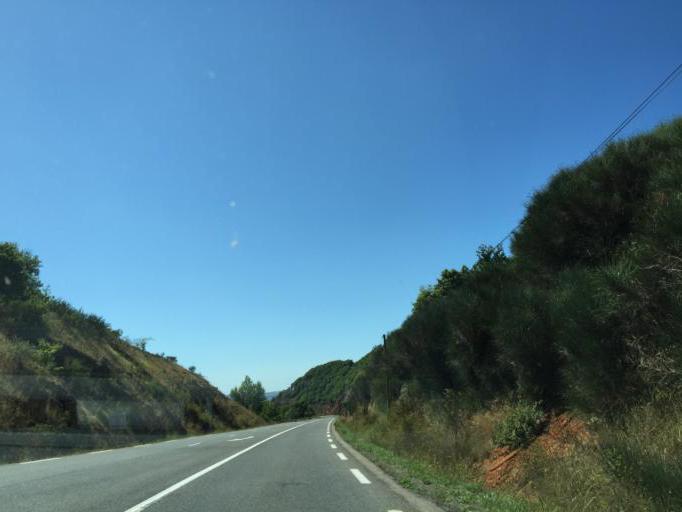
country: FR
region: Midi-Pyrenees
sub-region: Departement de l'Aveyron
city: Creissels
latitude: 44.0156
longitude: 3.0515
